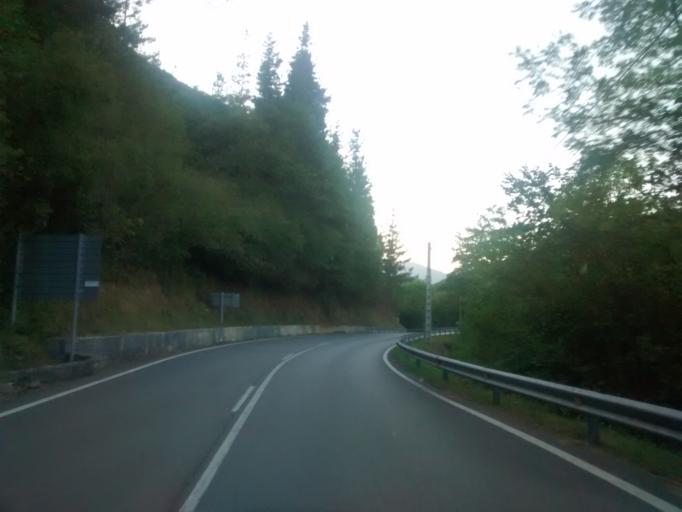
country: ES
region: Cantabria
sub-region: Provincia de Cantabria
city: Ruente
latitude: 43.1709
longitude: -4.2926
